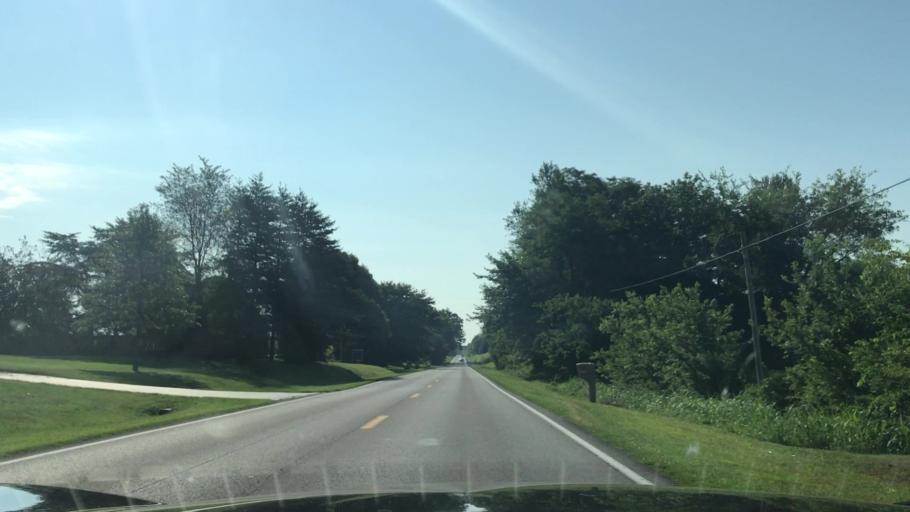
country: US
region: Kentucky
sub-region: Hart County
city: Horse Cave
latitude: 37.1742
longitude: -85.8637
